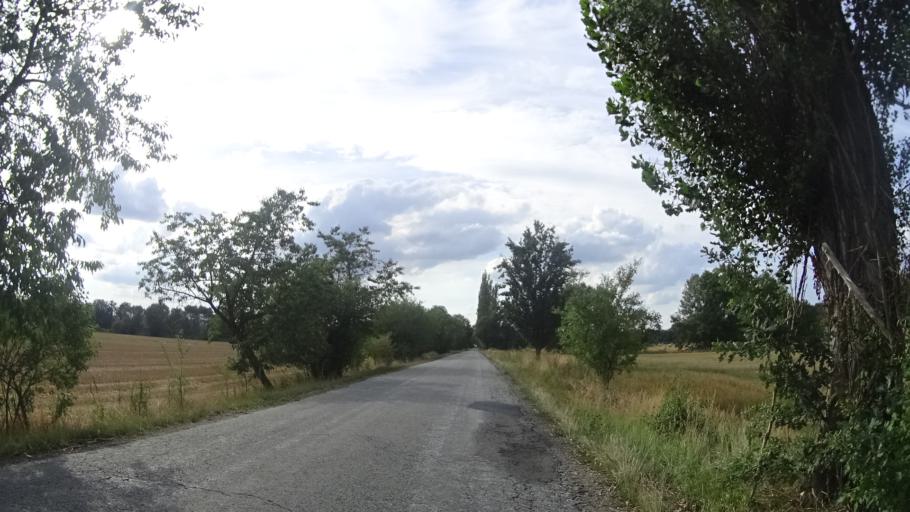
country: CZ
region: Olomoucky
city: Dubicko
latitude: 49.8005
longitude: 16.9504
